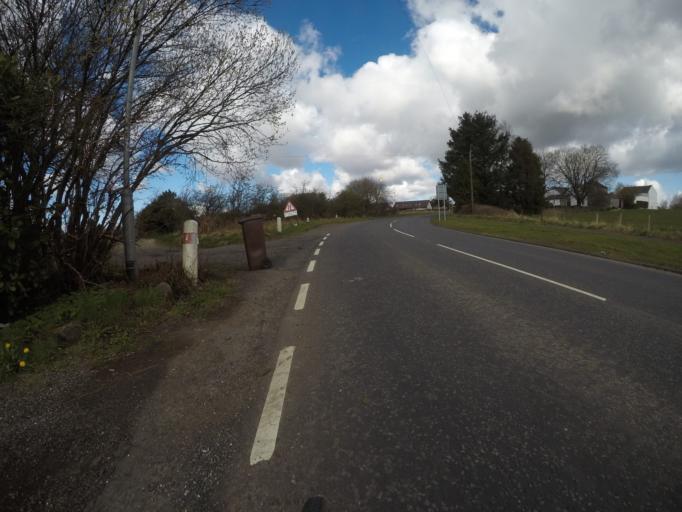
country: GB
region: Scotland
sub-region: North Ayrshire
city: Beith
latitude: 55.7453
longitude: -4.6288
